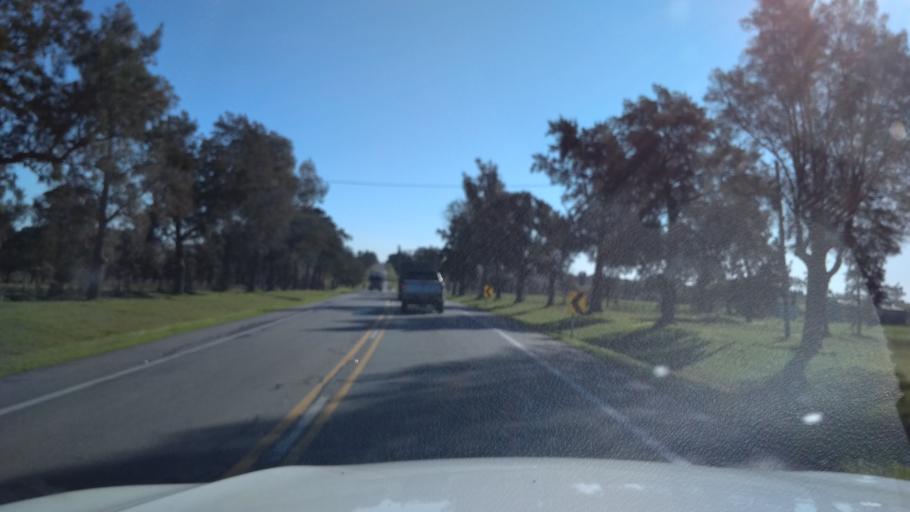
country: UY
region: Canelones
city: San Jacinto
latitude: -34.5419
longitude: -55.8870
